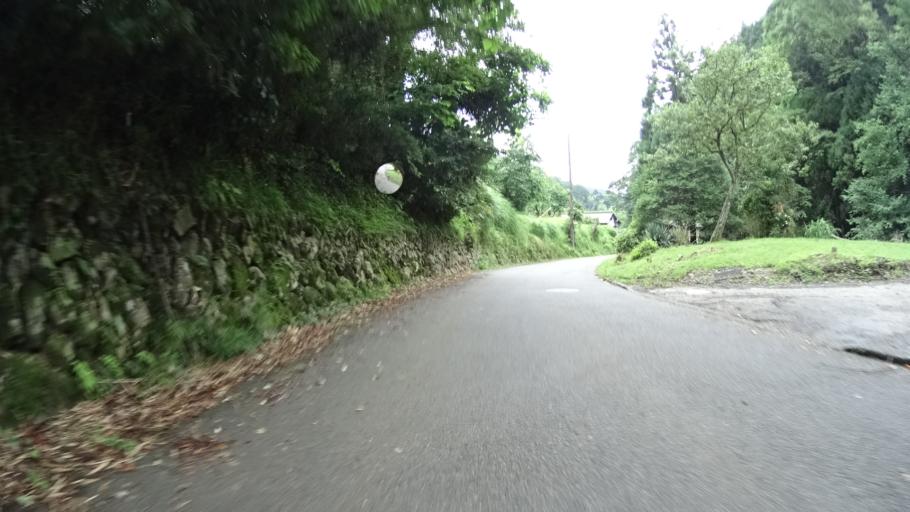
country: JP
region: Kanagawa
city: Atsugi
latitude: 35.4975
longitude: 139.2677
